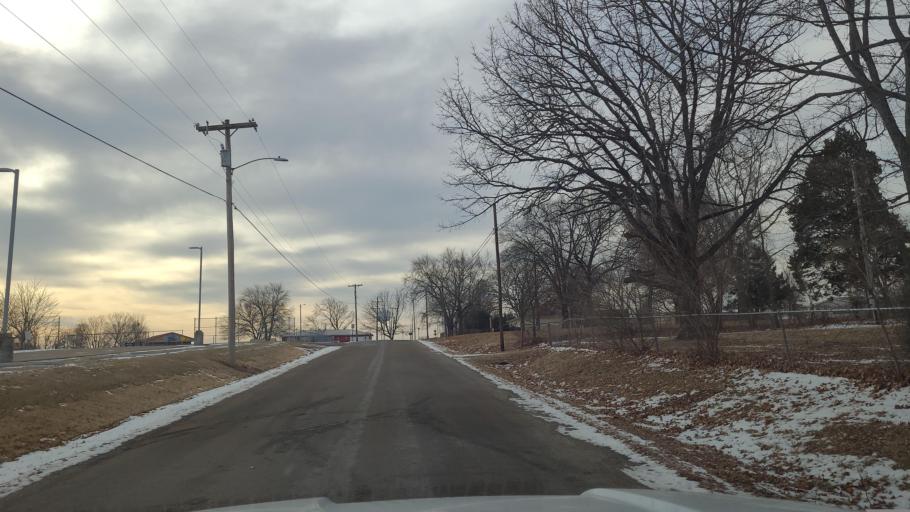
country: US
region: Kansas
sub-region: Douglas County
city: Lawrence
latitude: 39.0383
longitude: -95.3969
